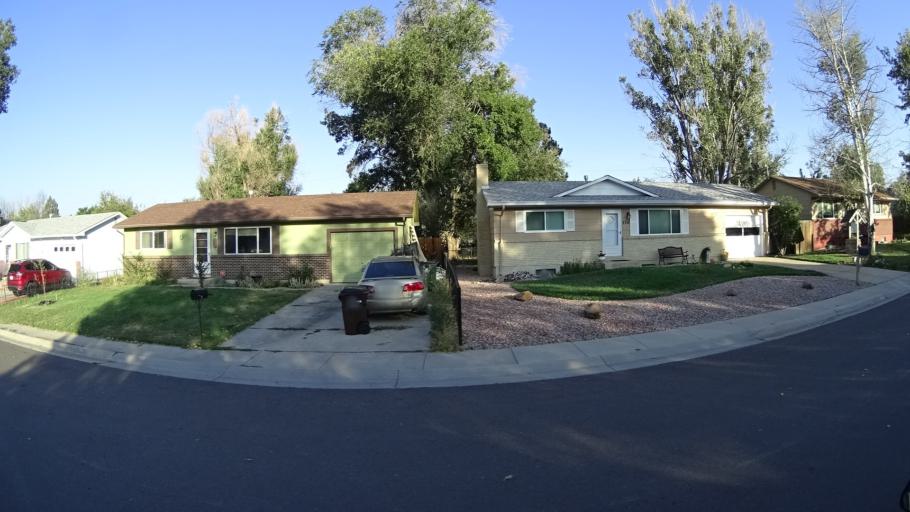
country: US
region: Colorado
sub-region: El Paso County
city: Cimarron Hills
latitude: 38.8945
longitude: -104.7617
